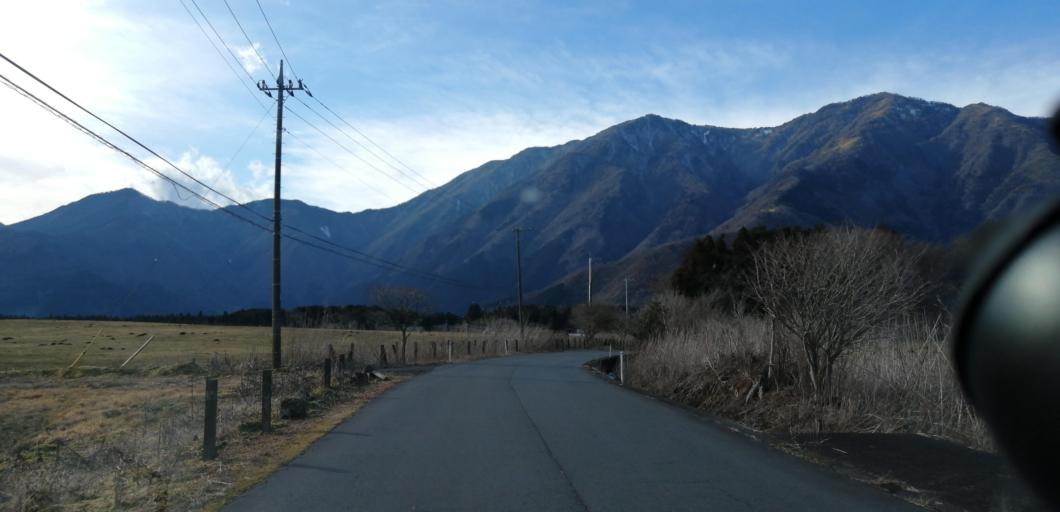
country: JP
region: Yamanashi
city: Fujikawaguchiko
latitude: 35.4035
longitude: 138.5944
